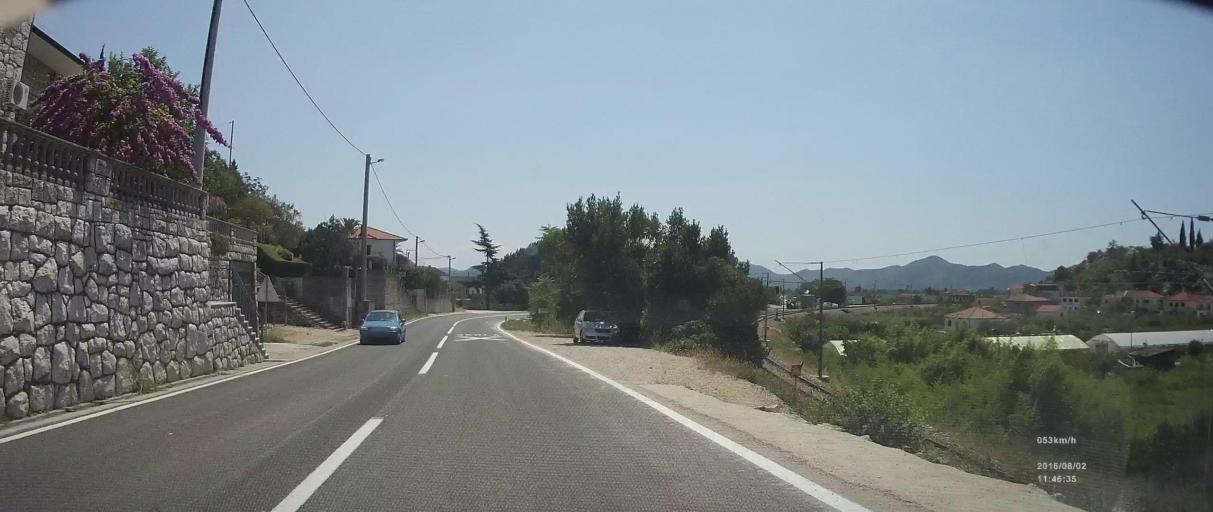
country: HR
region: Dubrovacko-Neretvanska
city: Komin
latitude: 43.0512
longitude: 17.4771
